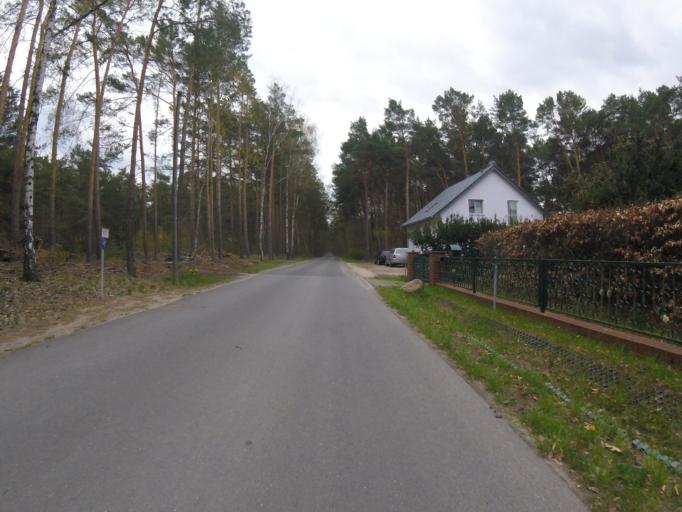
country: DE
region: Brandenburg
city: Schwerin
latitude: 52.1507
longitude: 13.6442
